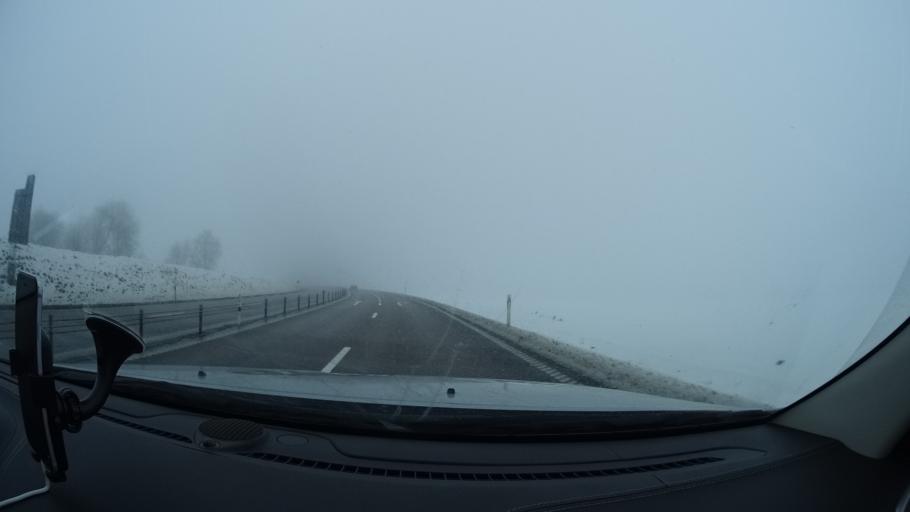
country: SE
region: OEstergoetland
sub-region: Mjolby Kommun
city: Mjolby
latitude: 58.3307
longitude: 15.0923
